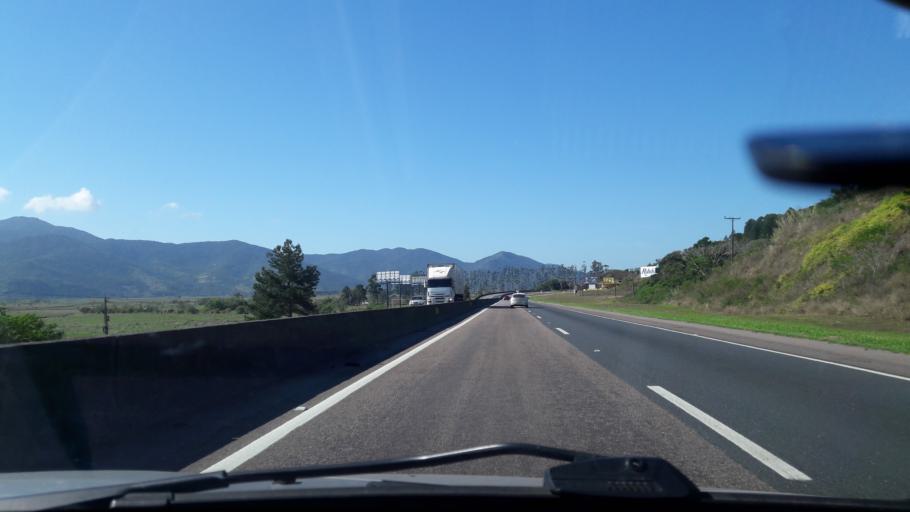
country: BR
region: Santa Catarina
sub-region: Tijucas
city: Tijucas
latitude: -27.3167
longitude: -48.6302
